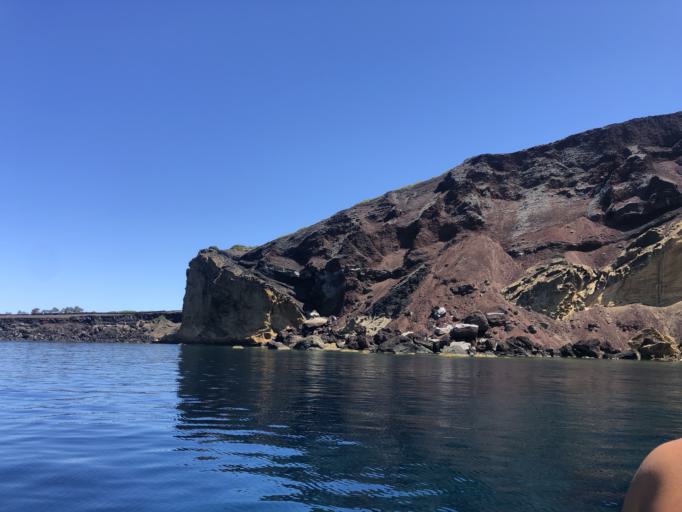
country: IT
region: Sicily
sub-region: Agrigento
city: Lampedusa
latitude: 35.8639
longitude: 12.8524
